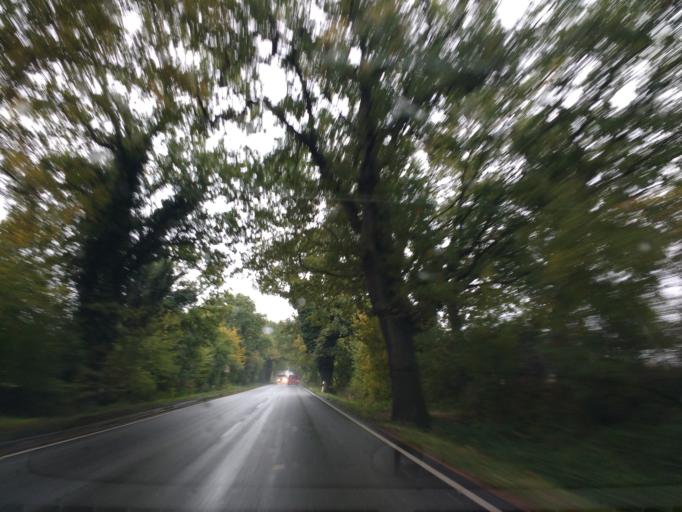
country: DE
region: Schleswig-Holstein
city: Susel
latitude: 54.1026
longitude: 10.6694
